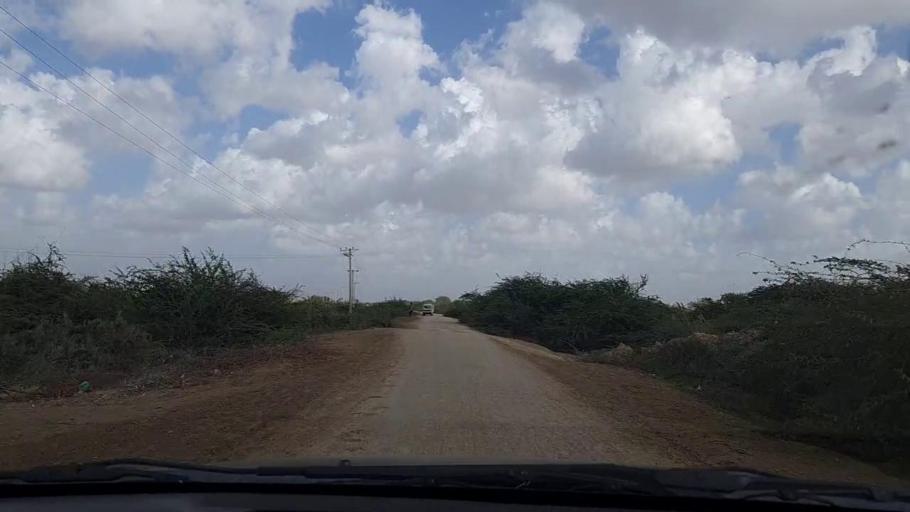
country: PK
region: Sindh
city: Keti Bandar
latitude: 24.0999
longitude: 67.5994
